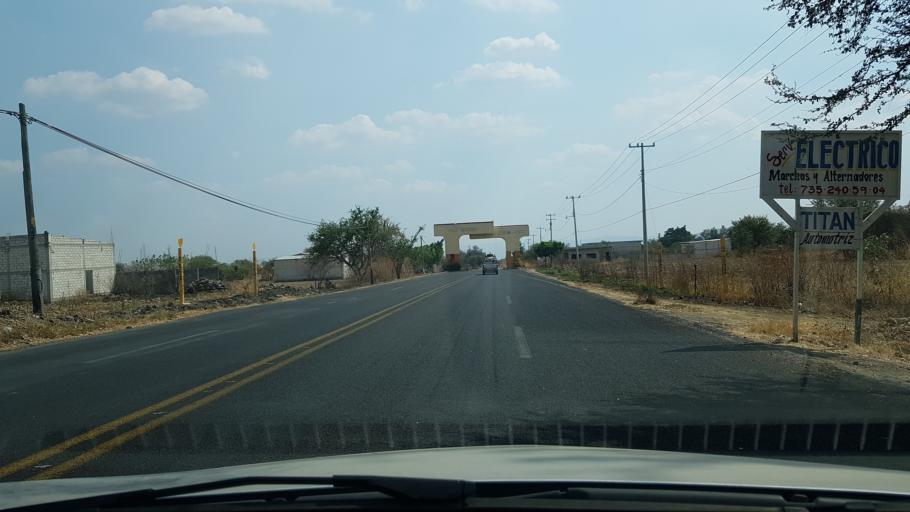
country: MX
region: Morelos
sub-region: Temoac
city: Huazulco
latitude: 18.7388
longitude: -98.7862
